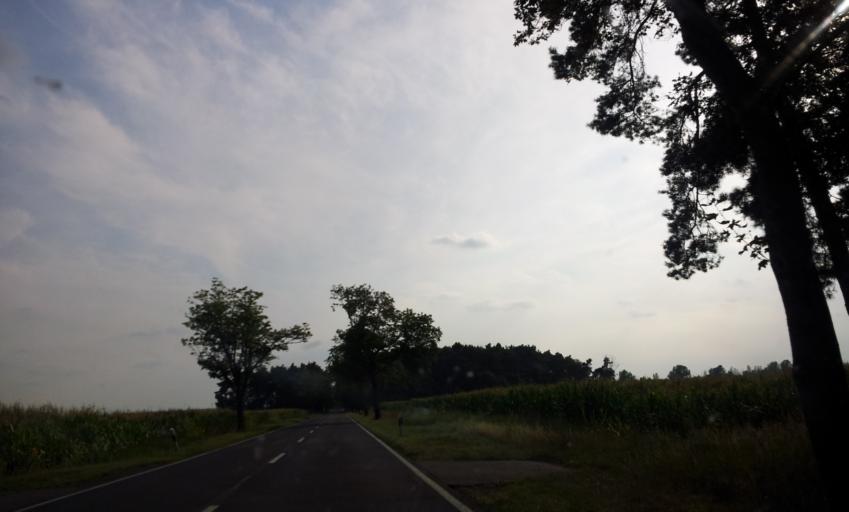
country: DE
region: Brandenburg
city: Treuenbrietzen
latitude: 52.1166
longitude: 12.9726
